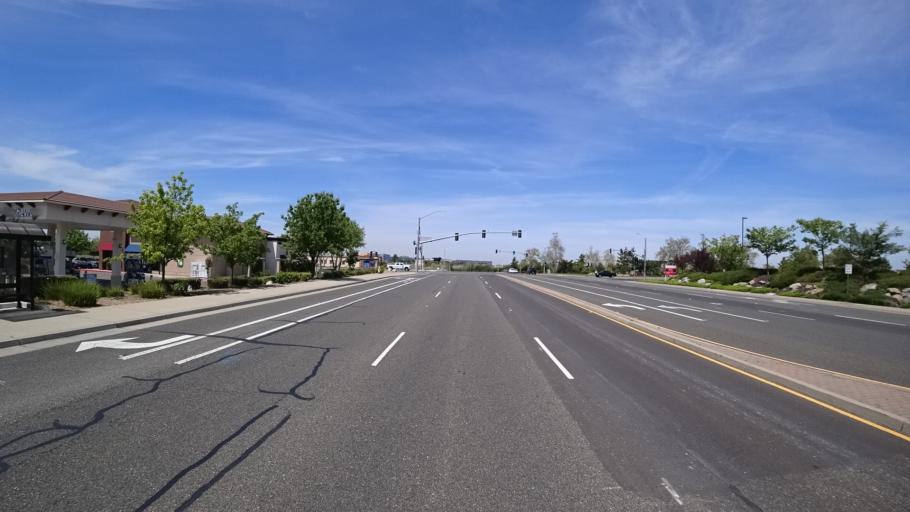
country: US
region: California
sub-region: Placer County
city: Rocklin
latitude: 38.8143
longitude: -121.2862
